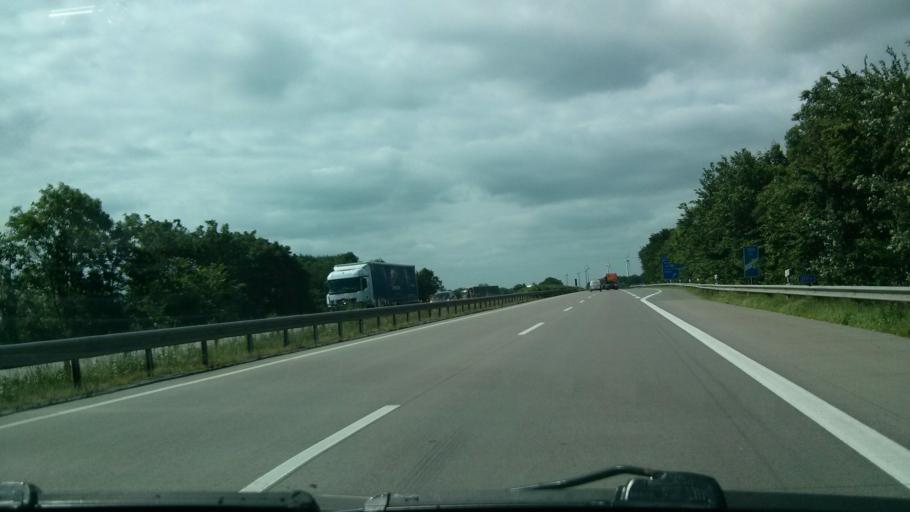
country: DE
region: Lower Saxony
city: Loxstedt
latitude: 53.4672
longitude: 8.6043
